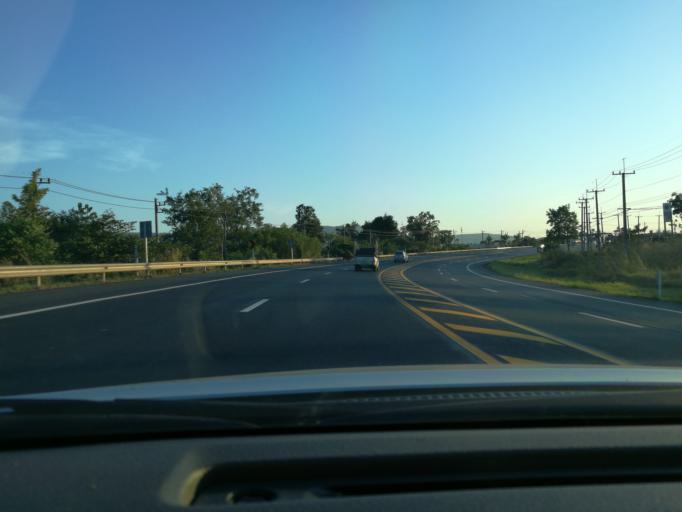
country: TH
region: Phitsanulok
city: Wang Thong
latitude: 16.8577
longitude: 100.4804
